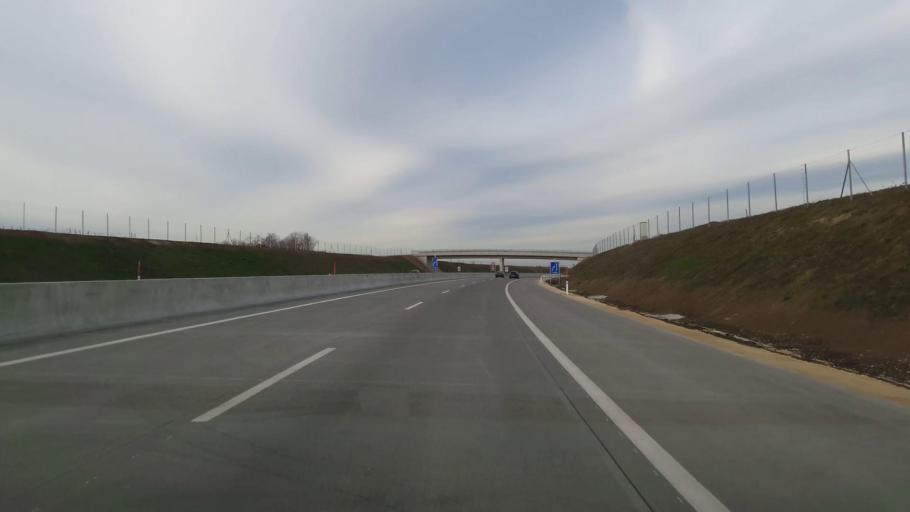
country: AT
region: Lower Austria
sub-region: Politischer Bezirk Mistelbach
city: Herrnbaumgarten
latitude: 48.6992
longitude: 16.6525
